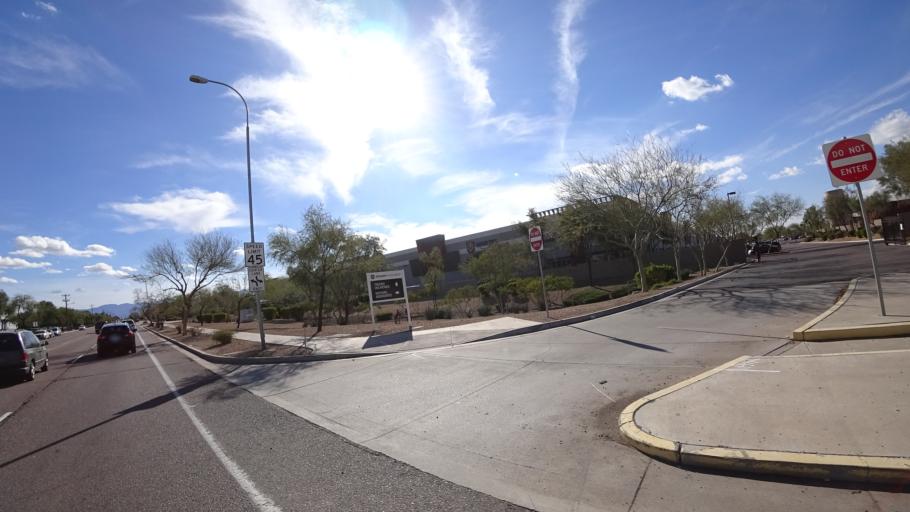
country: US
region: Arizona
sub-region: Maricopa County
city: Tolleson
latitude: 33.4581
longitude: -112.2210
